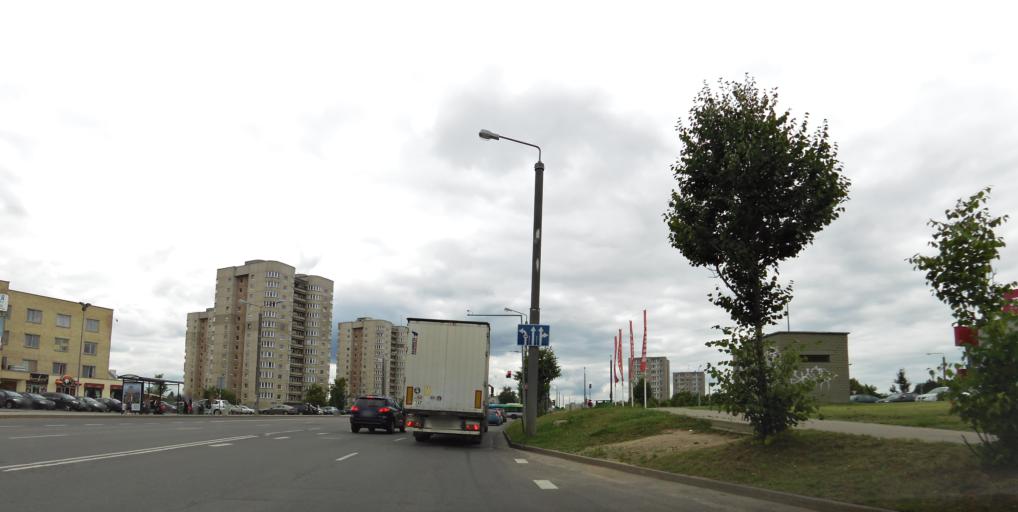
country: LT
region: Vilnius County
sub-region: Vilnius
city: Fabijoniskes
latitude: 54.7308
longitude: 25.2465
